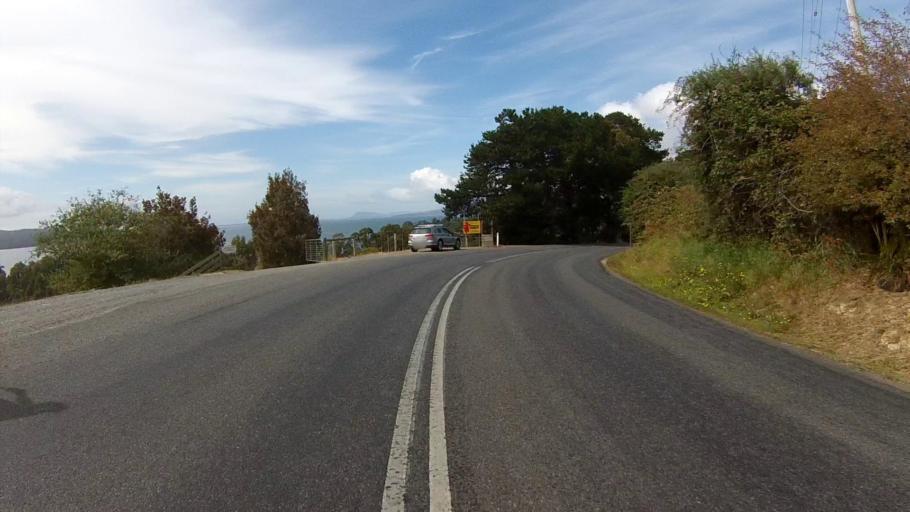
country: AU
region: Tasmania
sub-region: Kingborough
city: Kettering
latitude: -43.1421
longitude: 147.2435
